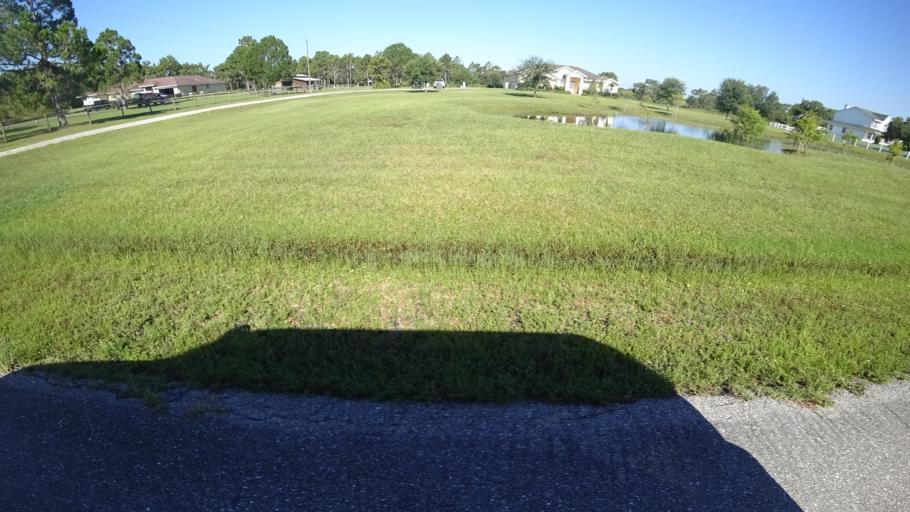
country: US
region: Florida
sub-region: Sarasota County
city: The Meadows
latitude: 27.4105
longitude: -82.3121
